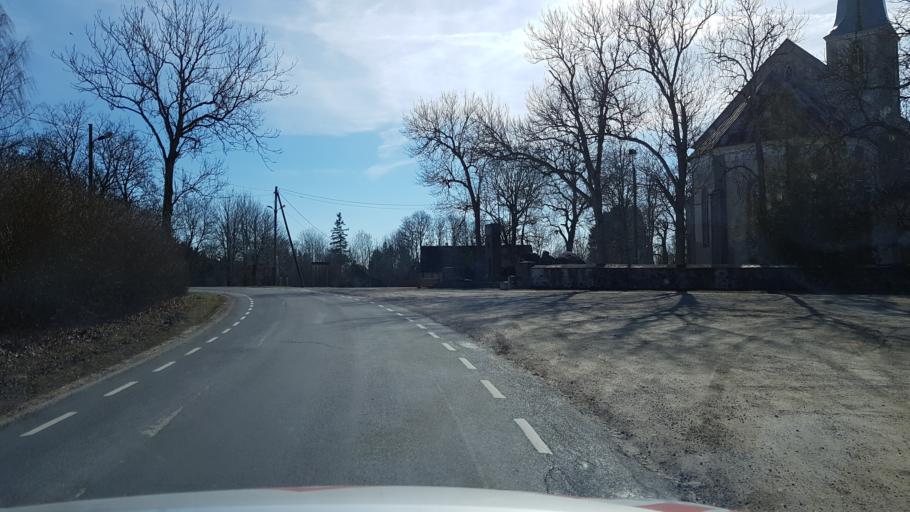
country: EE
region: Harju
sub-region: Nissi vald
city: Riisipere
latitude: 59.1043
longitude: 24.3108
